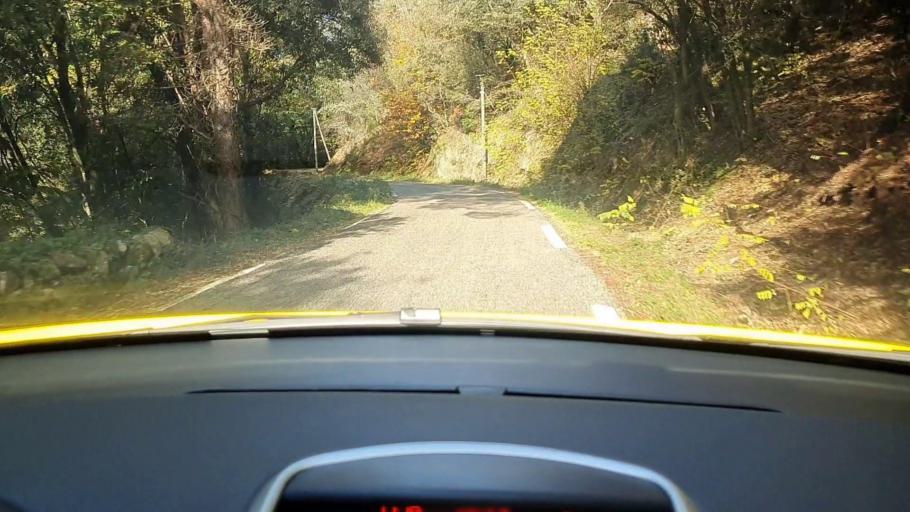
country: FR
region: Languedoc-Roussillon
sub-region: Departement du Gard
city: Lasalle
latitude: 44.0666
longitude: 3.8320
